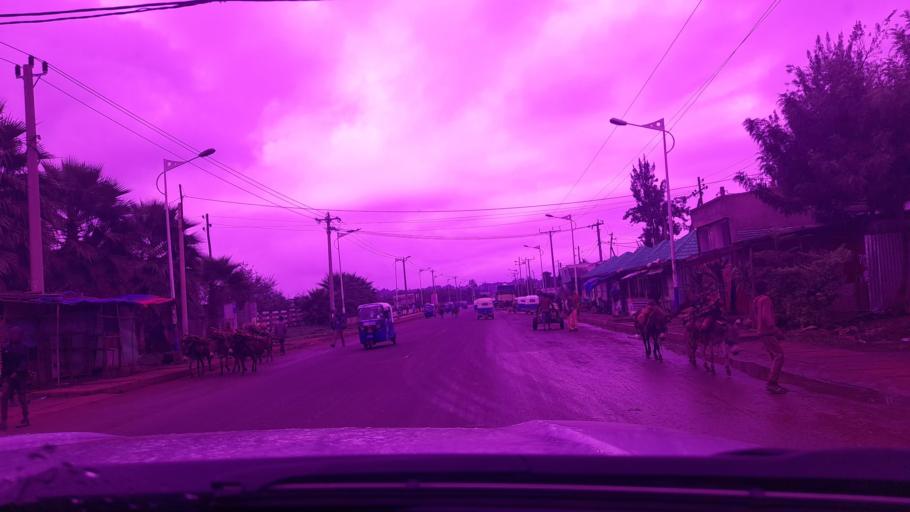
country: ET
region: Oromiya
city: Jima
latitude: 7.6580
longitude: 36.8435
